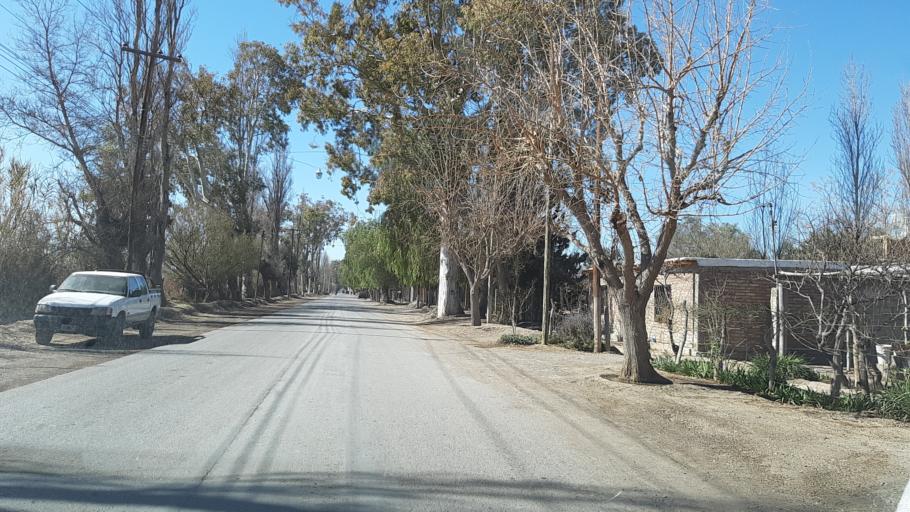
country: AR
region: San Juan
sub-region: Departamento de Zonda
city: Zonda
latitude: -31.4695
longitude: -68.7471
